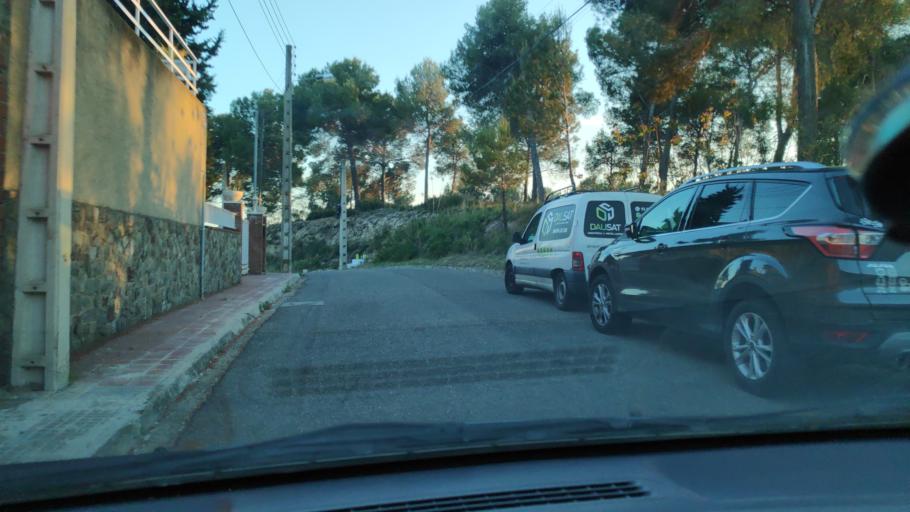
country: ES
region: Catalonia
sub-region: Provincia de Barcelona
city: Sant Quirze del Valles
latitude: 41.5304
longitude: 2.0495
